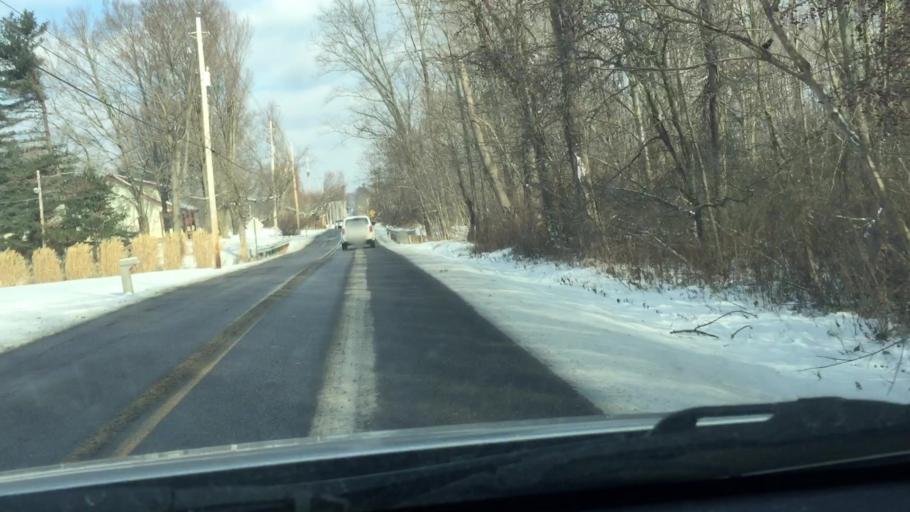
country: US
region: Ohio
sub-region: Mahoning County
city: Boardman
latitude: 41.0047
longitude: -80.7114
